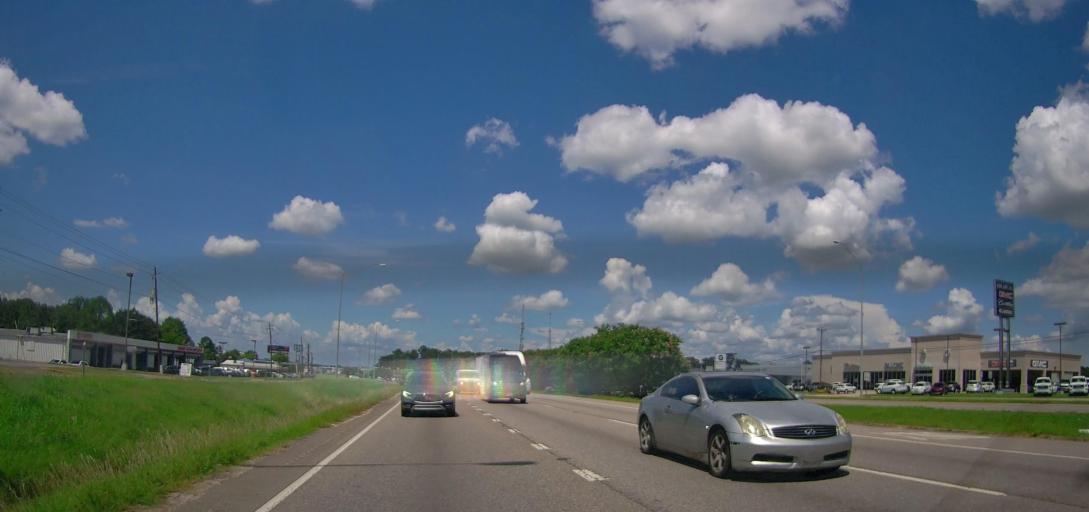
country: US
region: Alabama
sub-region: Montgomery County
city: Montgomery
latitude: 32.3683
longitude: -86.2108
